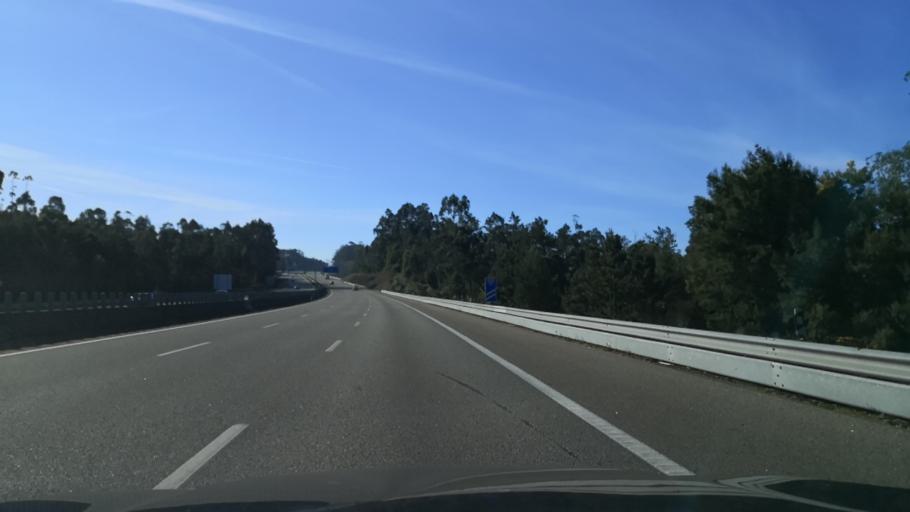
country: PT
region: Aveiro
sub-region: Santa Maria da Feira
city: Rio Meao
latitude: 40.9382
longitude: -8.5737
